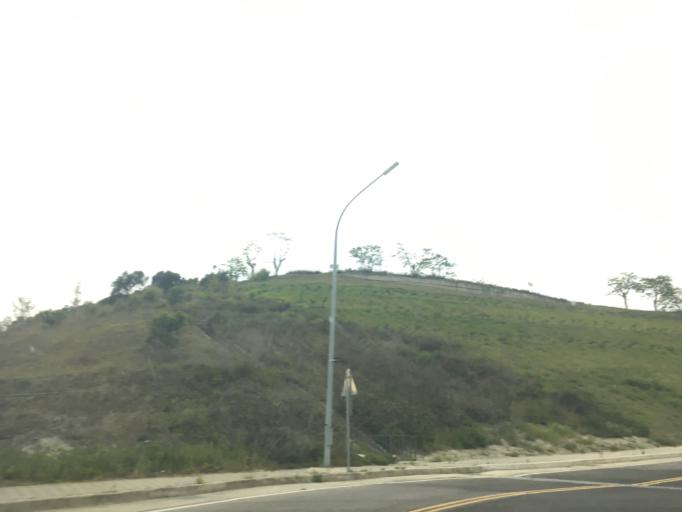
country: TW
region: Taiwan
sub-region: Taichung City
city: Taichung
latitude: 24.1721
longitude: 120.7687
